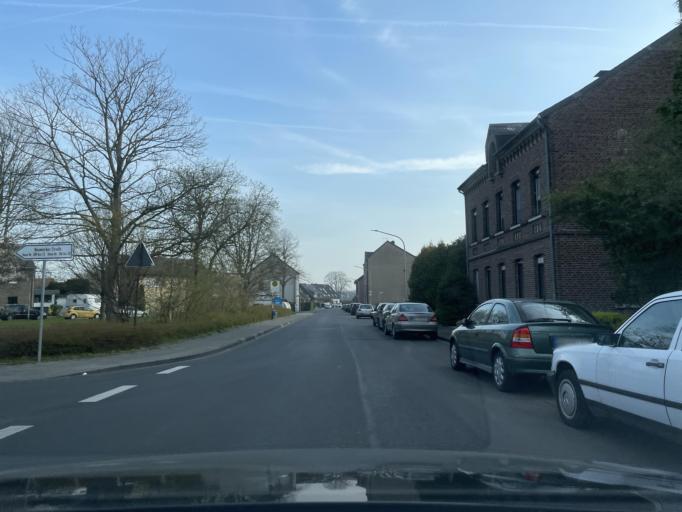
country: DE
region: North Rhine-Westphalia
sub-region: Regierungsbezirk Dusseldorf
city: Viersen
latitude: 51.2332
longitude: 6.4279
